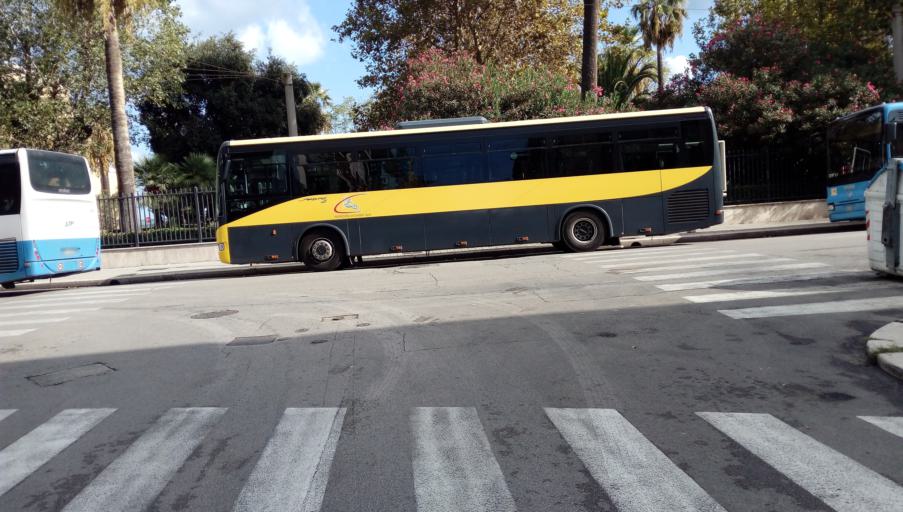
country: IT
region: Apulia
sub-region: Provincia di Bari
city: Bari
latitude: 41.1183
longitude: 16.8878
